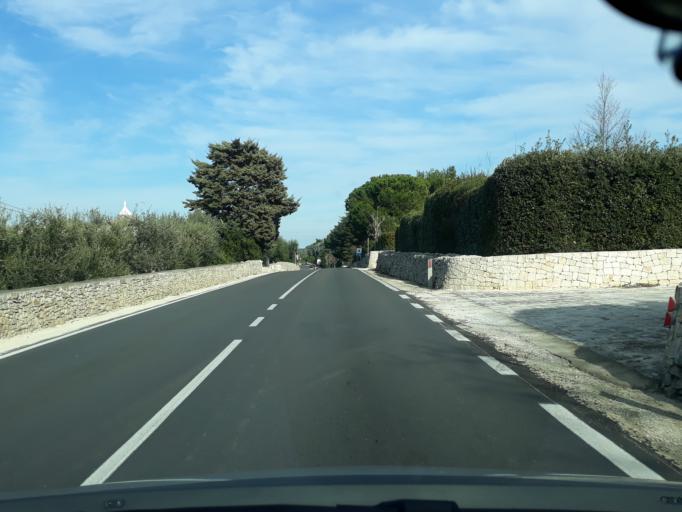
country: IT
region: Apulia
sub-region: Provincia di Brindisi
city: Lamie di Olimpie-Selva
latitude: 40.7879
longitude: 17.3435
